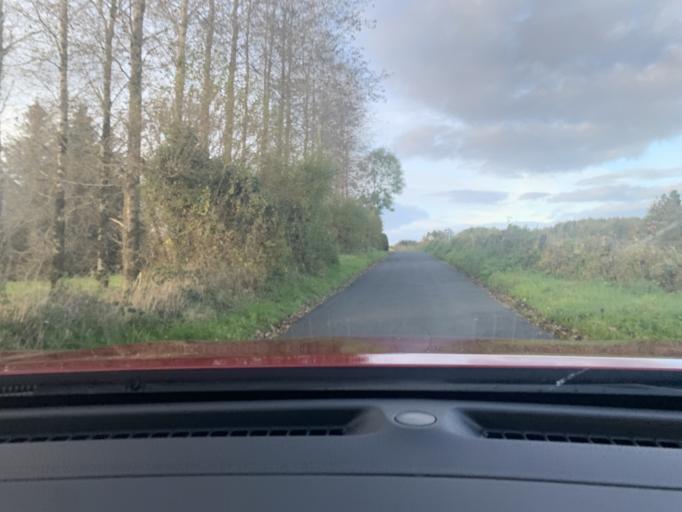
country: IE
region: Connaught
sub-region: Roscommon
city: Ballaghaderreen
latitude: 53.9177
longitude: -8.5922
